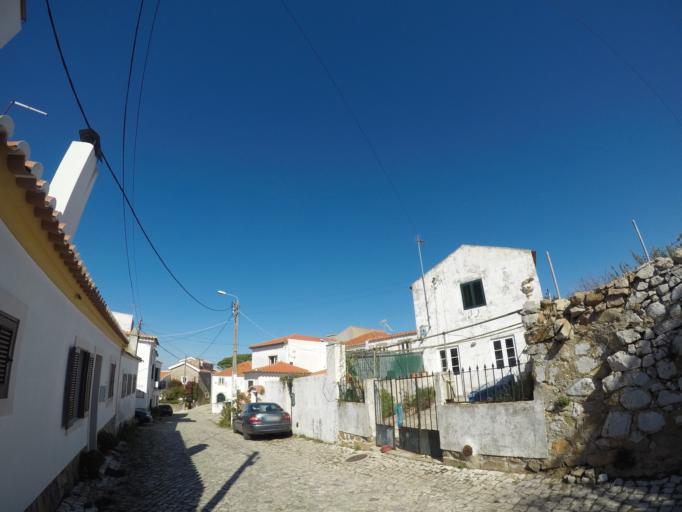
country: PT
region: Lisbon
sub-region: Sintra
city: Colares
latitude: 38.7863
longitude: -9.4760
